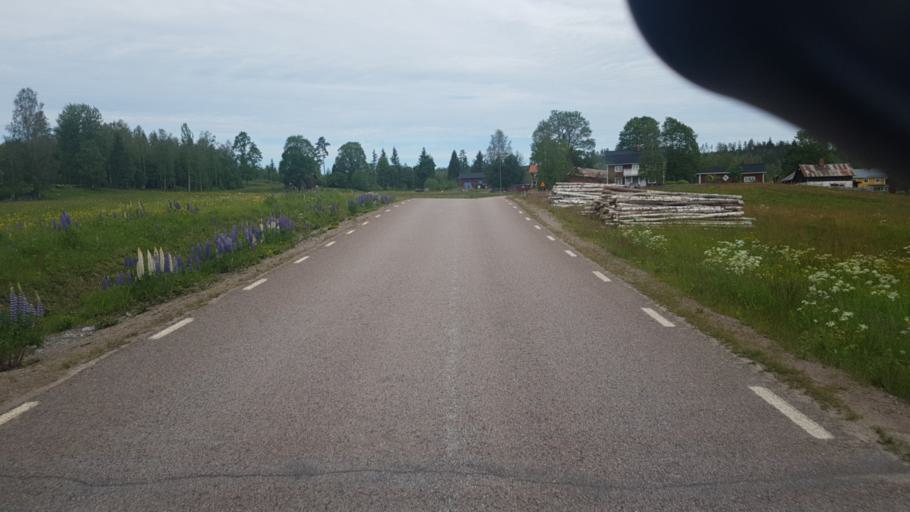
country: SE
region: Vaermland
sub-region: Arvika Kommun
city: Arvika
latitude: 59.7705
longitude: 12.8209
